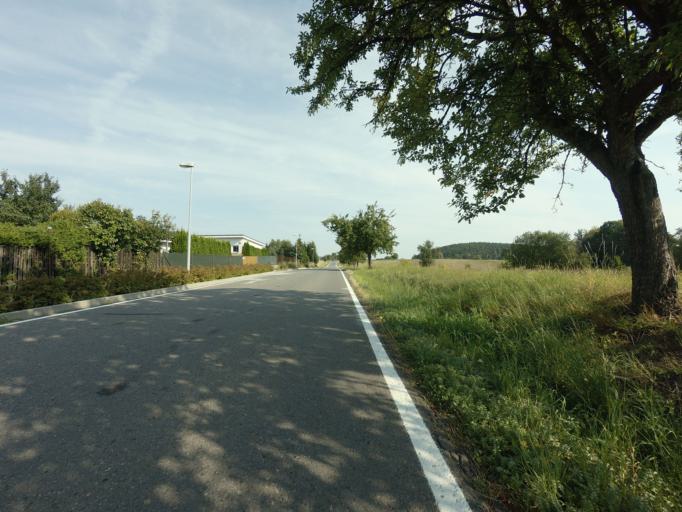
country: CZ
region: Jihocesky
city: Milevsko
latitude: 49.4625
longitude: 14.3628
